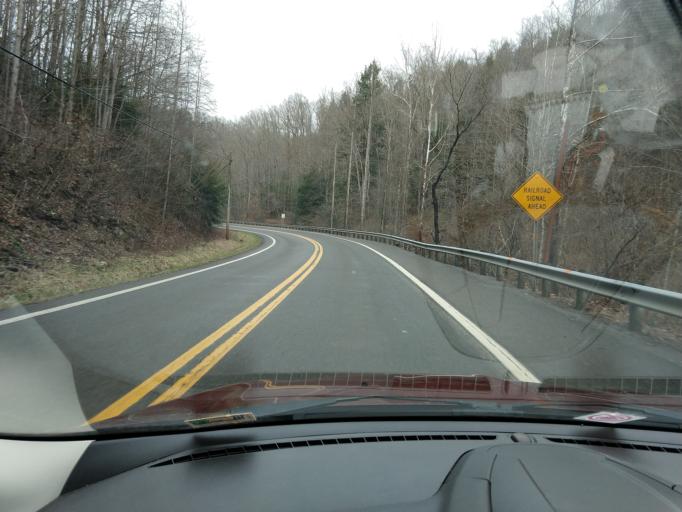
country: US
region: West Virginia
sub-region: Wyoming County
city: Pineville
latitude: 37.5663
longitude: -81.5319
